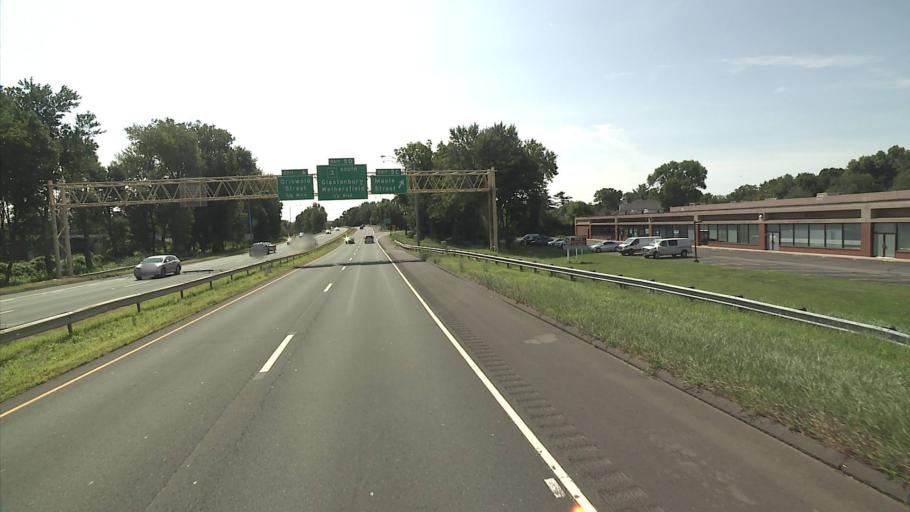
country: US
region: Connecticut
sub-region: Hartford County
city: Glastonbury
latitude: 41.7348
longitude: -72.6255
